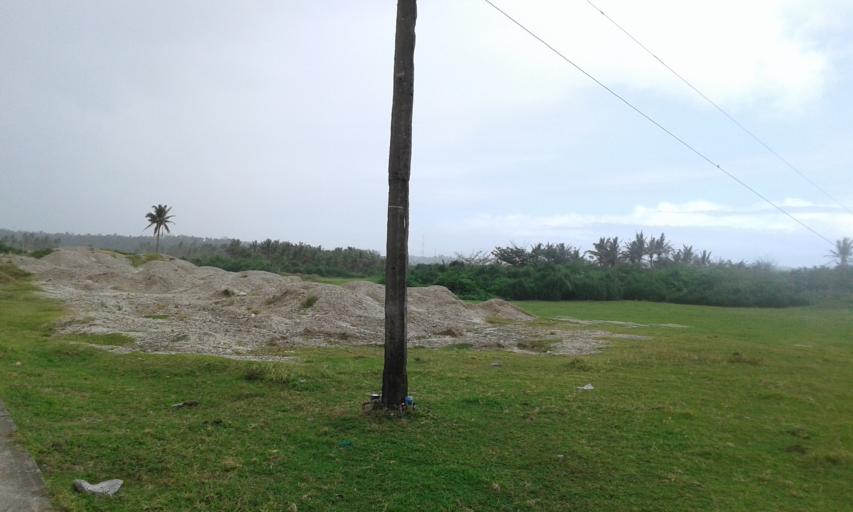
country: PH
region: Bicol
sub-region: Province of Sorsogon
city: Gubat
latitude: 12.9012
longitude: 124.1176
